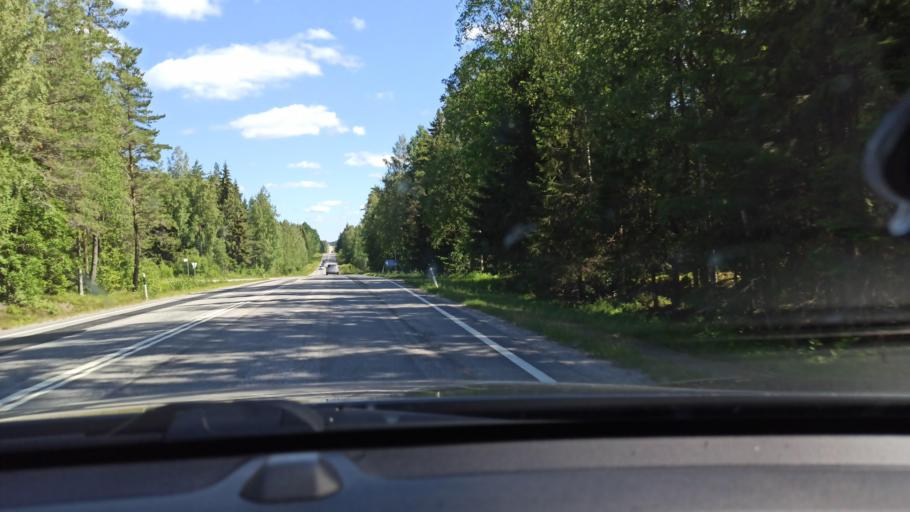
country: FI
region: Ostrobothnia
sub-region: Vaasa
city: Malax
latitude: 62.9850
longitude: 21.6297
